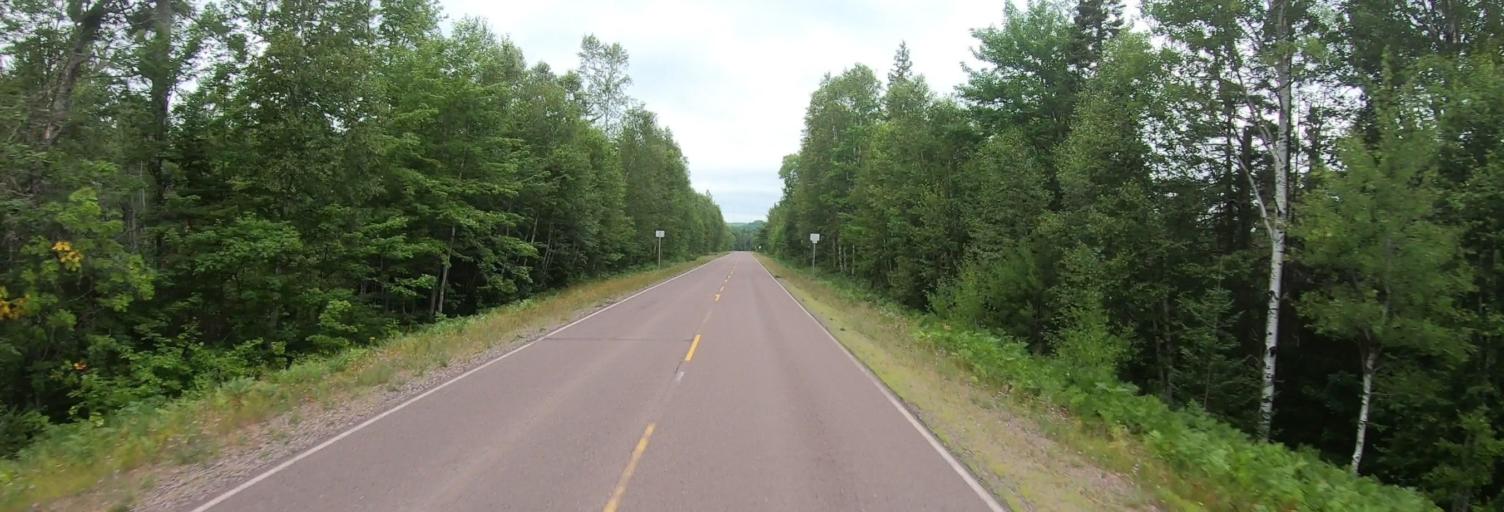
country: US
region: Michigan
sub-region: Keweenaw County
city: Eagle River
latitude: 47.2863
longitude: -88.3106
